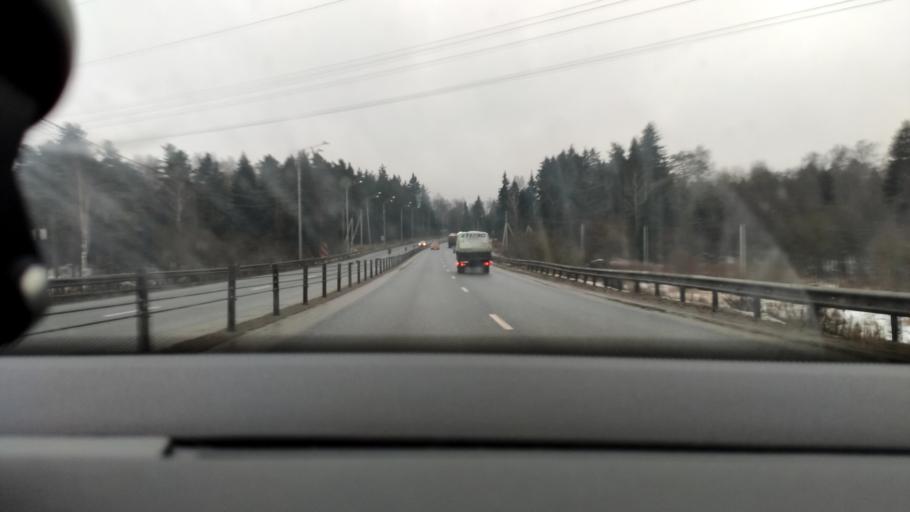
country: RU
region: Moskovskaya
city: Sergiyev Posad
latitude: 56.2653
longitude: 38.1253
